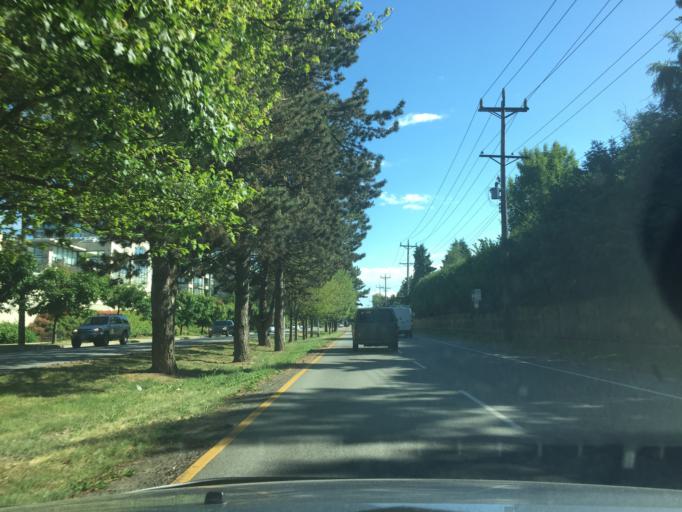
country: CA
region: British Columbia
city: Richmond
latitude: 49.1685
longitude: -123.1246
